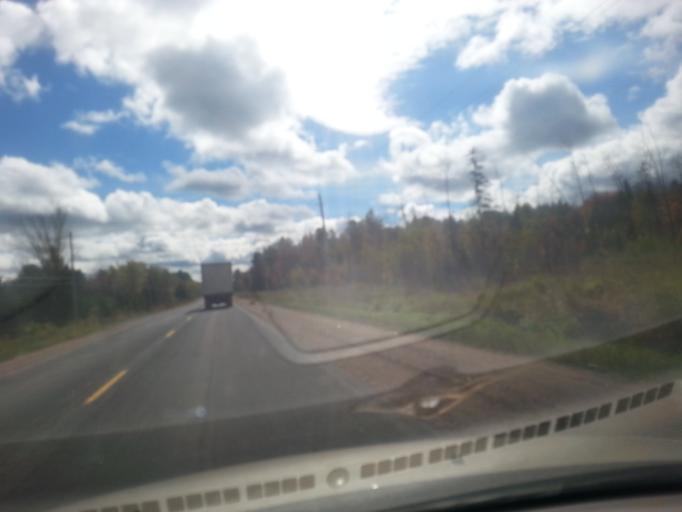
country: CA
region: Ontario
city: Pembroke
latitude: 45.6840
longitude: -77.0998
